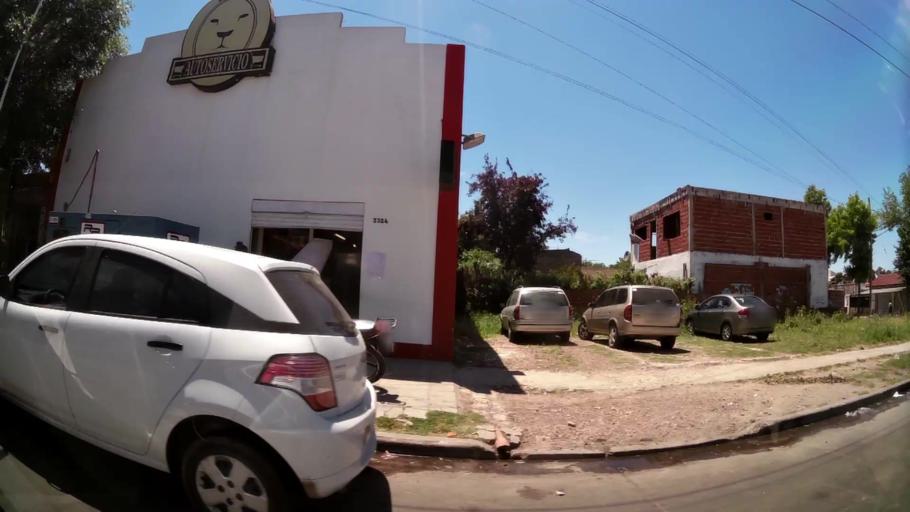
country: AR
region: Buenos Aires
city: Hurlingham
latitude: -34.5120
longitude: -58.7103
